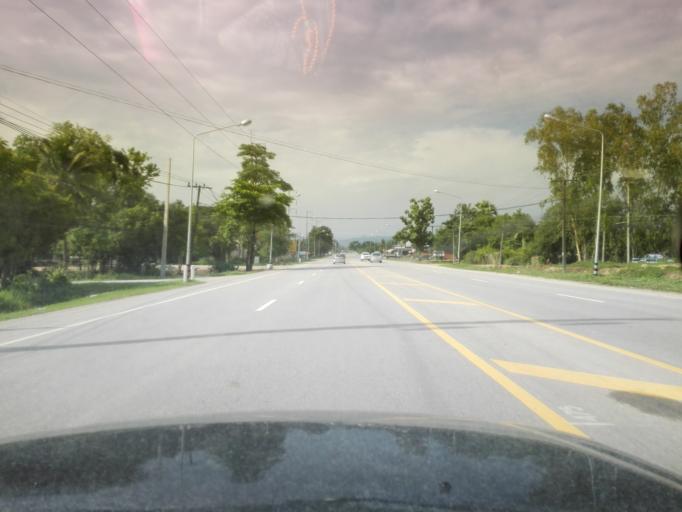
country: TH
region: Tak
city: Mae Sot
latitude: 16.7428
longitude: 98.5765
